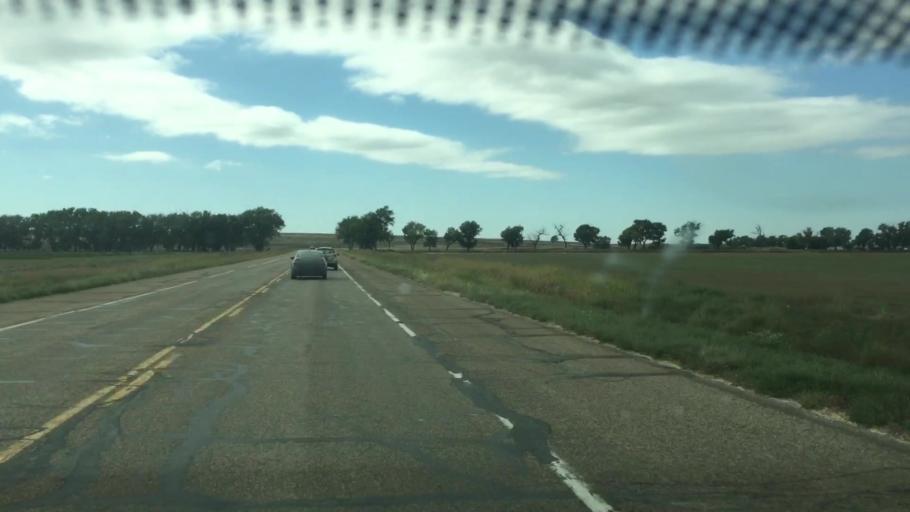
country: US
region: Colorado
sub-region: Prowers County
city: Lamar
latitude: 38.0638
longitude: -102.3514
